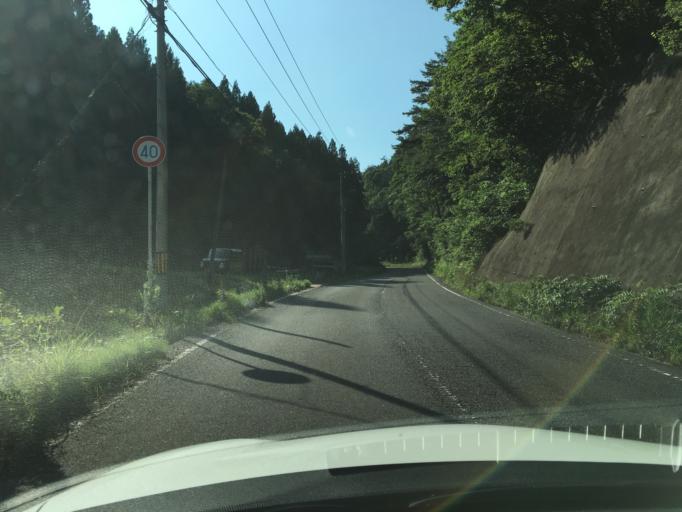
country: JP
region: Fukushima
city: Ishikawa
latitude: 37.1999
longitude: 140.4831
